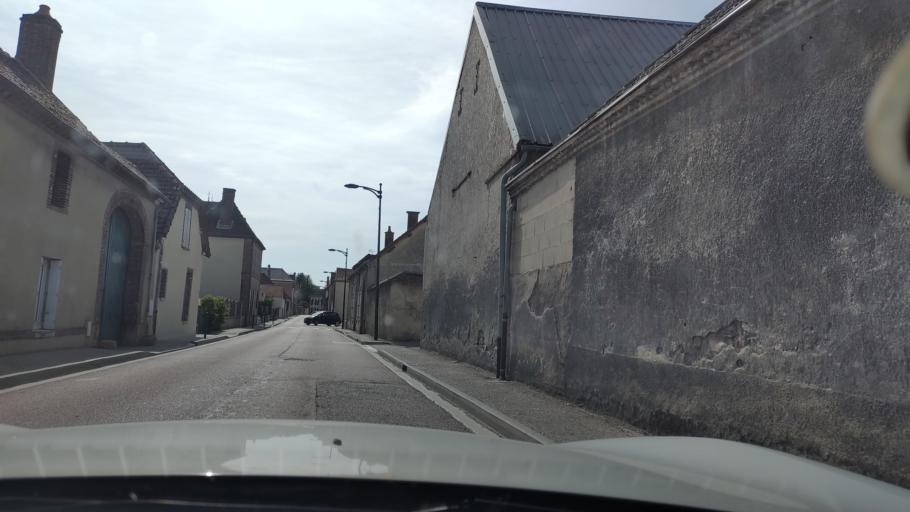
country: FR
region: Champagne-Ardenne
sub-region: Departement de l'Aube
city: Marigny-le-Chatel
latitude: 48.4029
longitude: 3.7377
